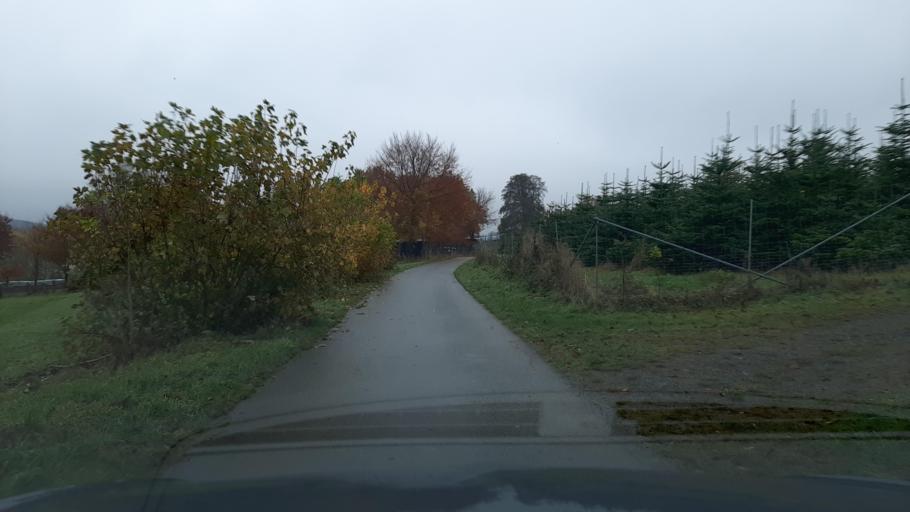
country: DE
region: North Rhine-Westphalia
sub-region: Regierungsbezirk Arnsberg
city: Olsberg
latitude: 51.2940
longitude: 8.5061
